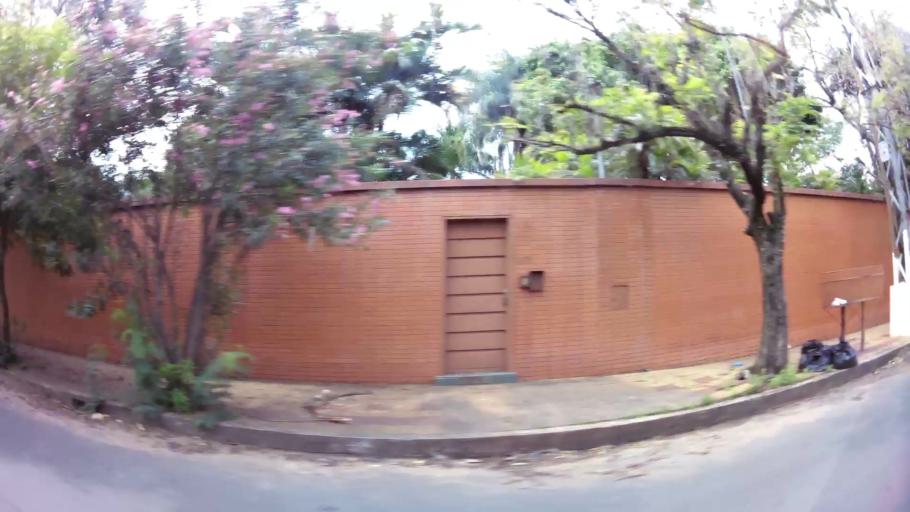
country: PY
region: Asuncion
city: Asuncion
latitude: -25.2901
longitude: -57.5799
